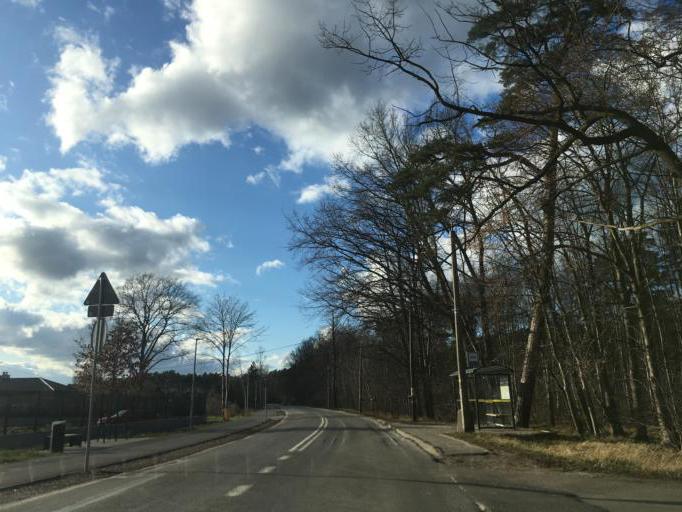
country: PL
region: Pomeranian Voivodeship
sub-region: Powiat gdanski
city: Cedry Wielkie
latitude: 54.3416
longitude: 18.8733
